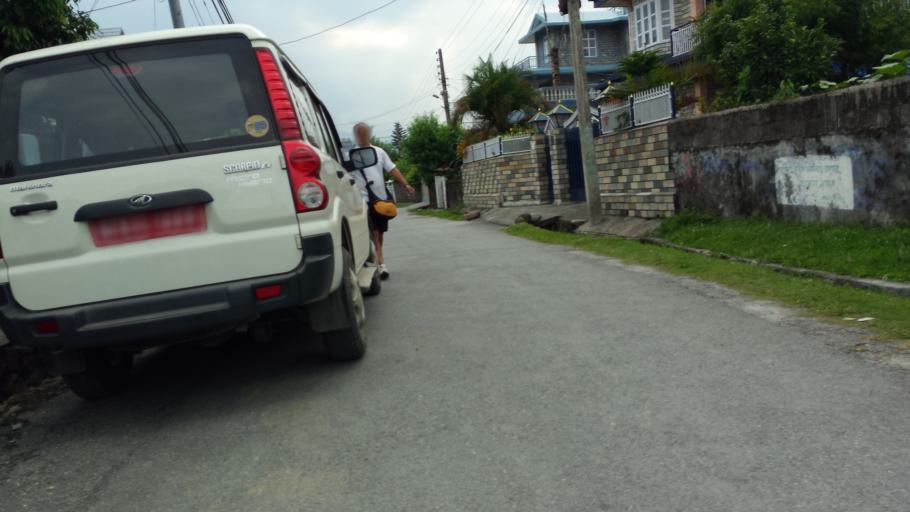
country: NP
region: Western Region
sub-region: Gandaki Zone
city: Pokhara
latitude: 28.2089
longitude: 83.9974
